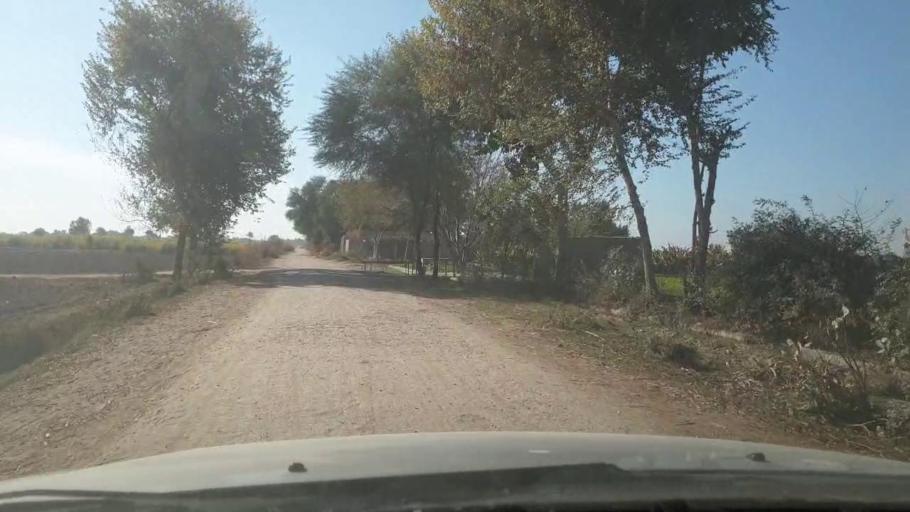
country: PK
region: Sindh
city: Ghotki
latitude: 27.9789
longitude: 69.1987
